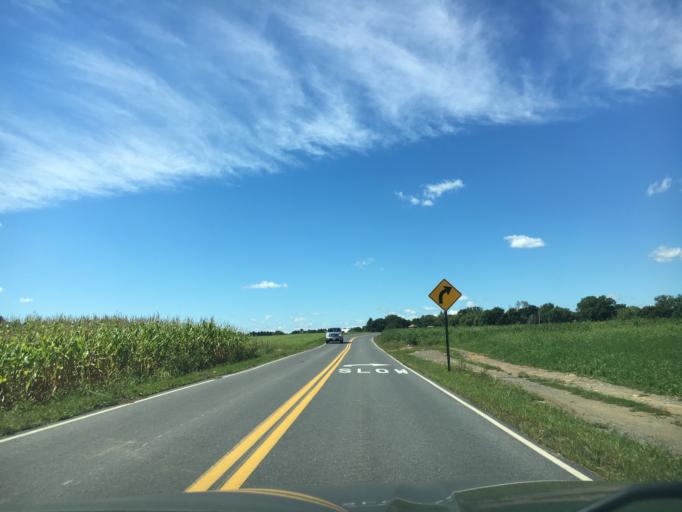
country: US
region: Pennsylvania
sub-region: Berks County
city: Topton
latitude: 40.5135
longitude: -75.6874
